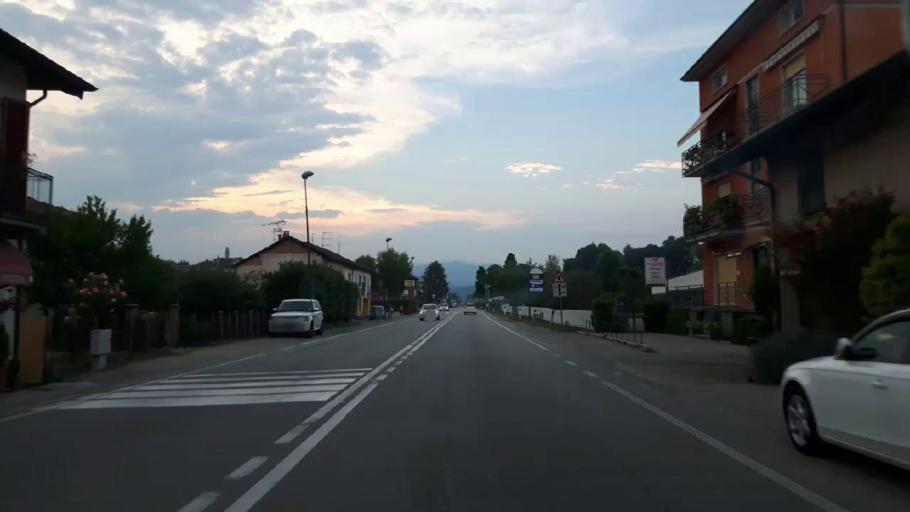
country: IT
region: Piedmont
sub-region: Provincia di Novara
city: Dormelletto
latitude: 45.7262
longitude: 8.5805
